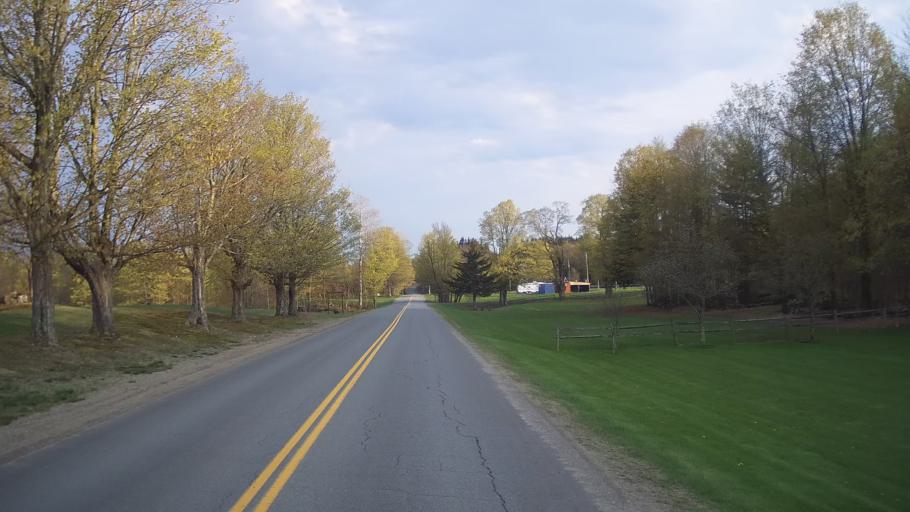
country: US
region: Vermont
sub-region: Orleans County
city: Newport
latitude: 44.9173
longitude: -72.4312
